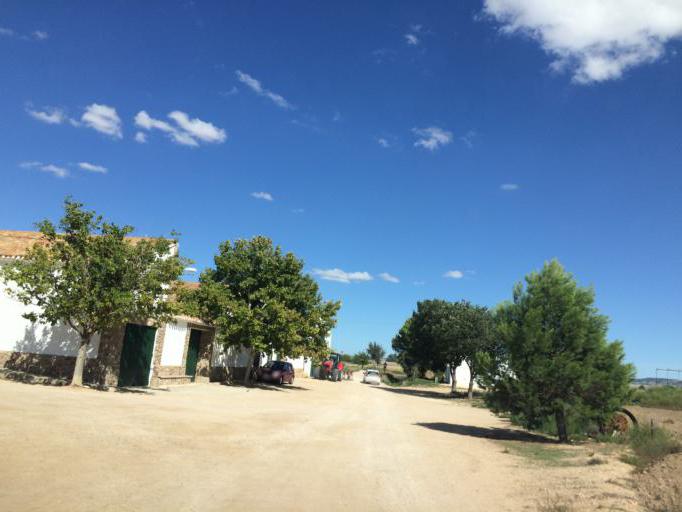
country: ES
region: Castille-La Mancha
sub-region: Provincia de Albacete
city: Albacete
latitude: 38.9374
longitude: -1.8390
